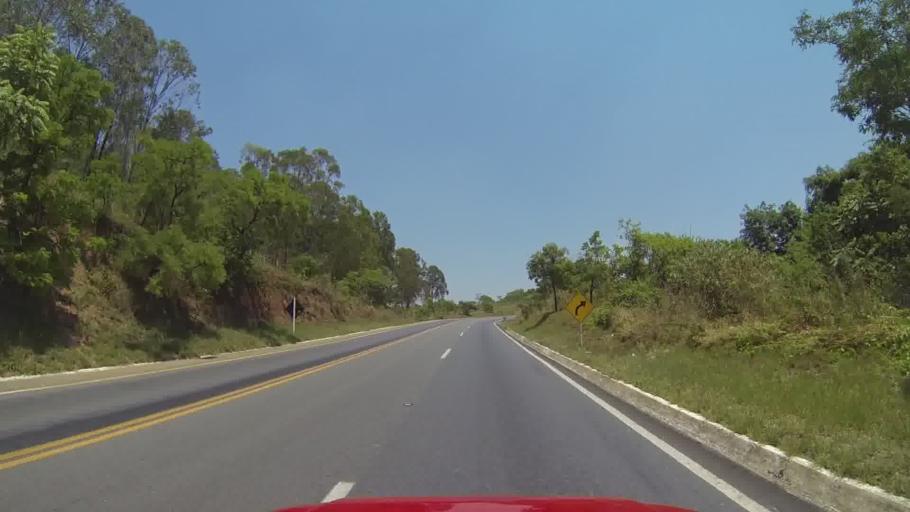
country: BR
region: Minas Gerais
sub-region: Itapecerica
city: Itapecerica
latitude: -20.2991
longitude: -45.1967
